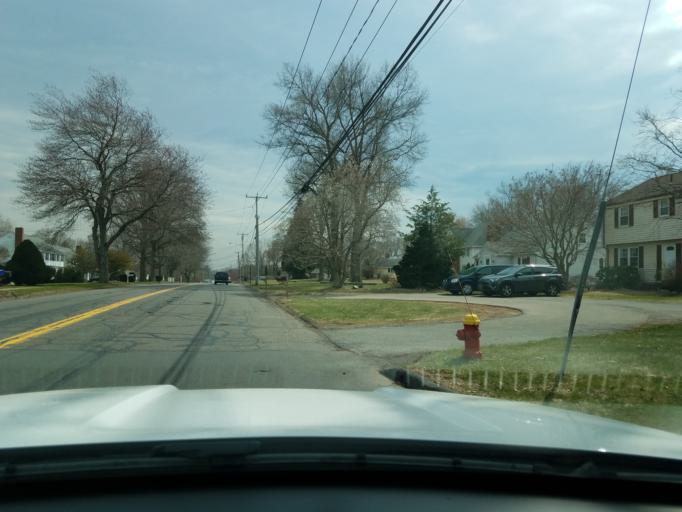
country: US
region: Connecticut
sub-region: Hartford County
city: Newington
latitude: 41.6735
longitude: -72.6891
